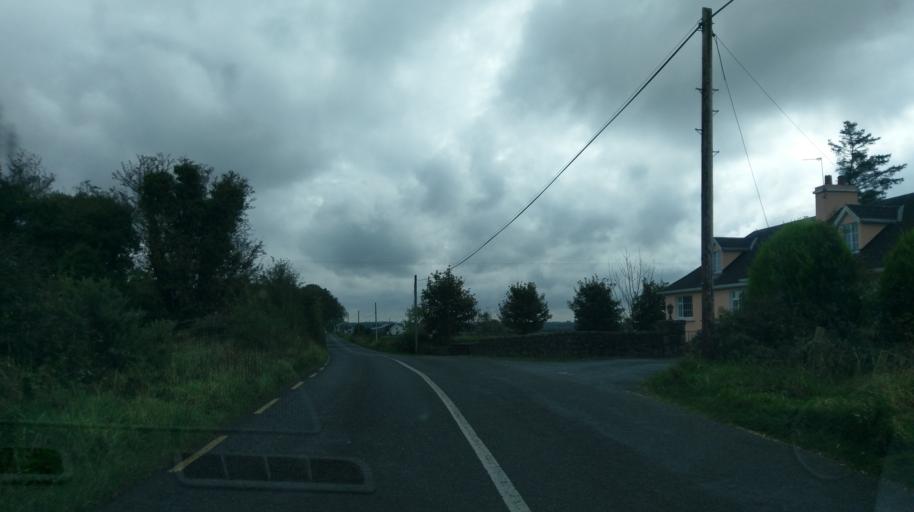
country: IE
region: Connaught
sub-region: County Galway
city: Ballinasloe
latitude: 53.4332
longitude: -8.4269
